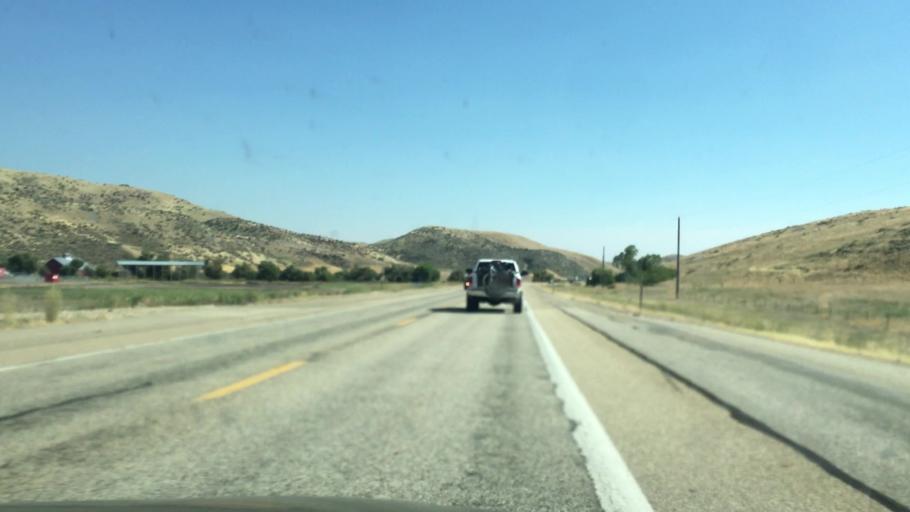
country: US
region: Idaho
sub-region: Ada County
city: Eagle
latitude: 43.7967
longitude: -116.2646
